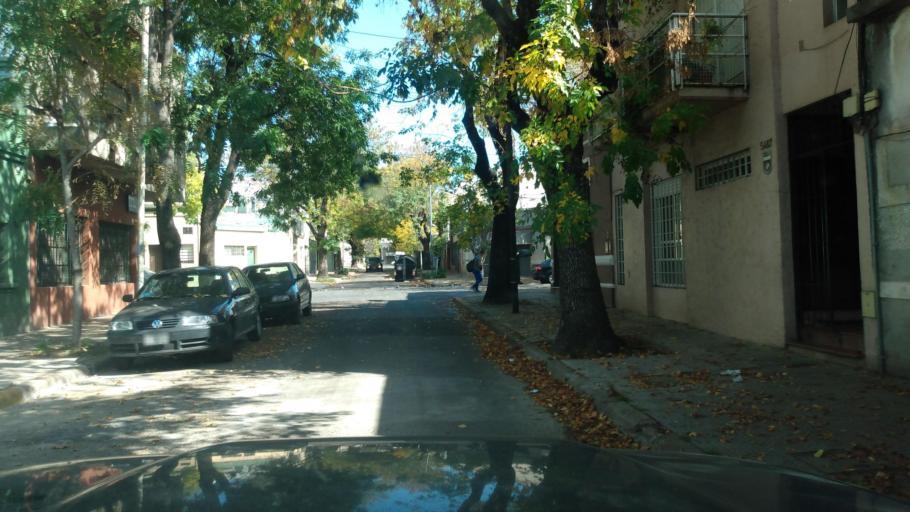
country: AR
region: Buenos Aires
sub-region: Partido de General San Martin
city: General San Martin
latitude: -34.5647
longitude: -58.4971
